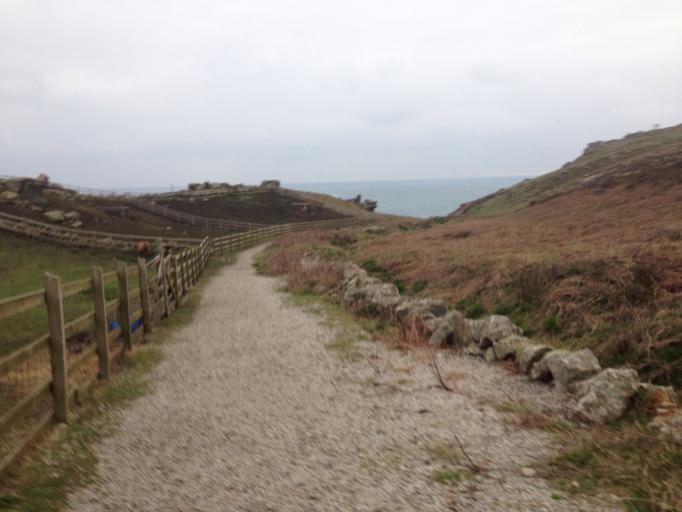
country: GB
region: England
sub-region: Cornwall
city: Sennen
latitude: 50.0627
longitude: -5.7115
